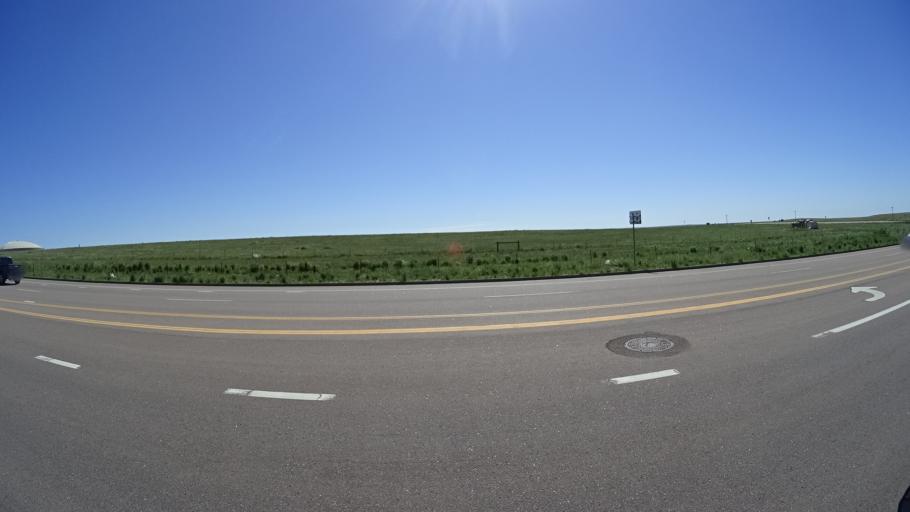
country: US
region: Colorado
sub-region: El Paso County
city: Cimarron Hills
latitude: 38.8397
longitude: -104.6829
